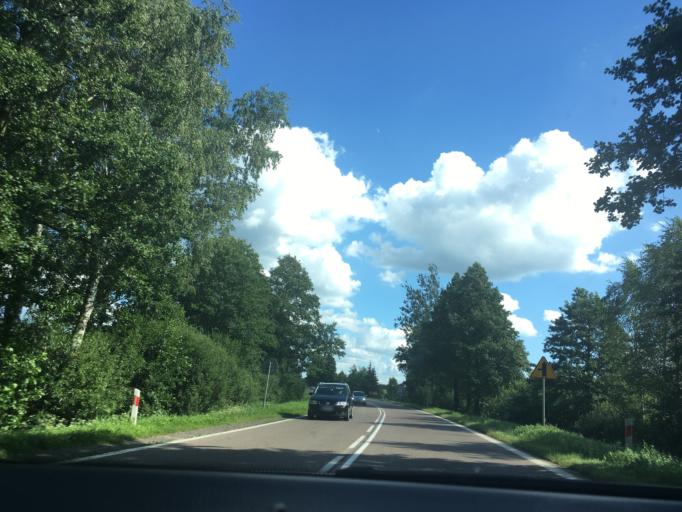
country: PL
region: Podlasie
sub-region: Powiat bialostocki
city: Dobrzyniewo Duze
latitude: 53.3395
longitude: 23.1021
